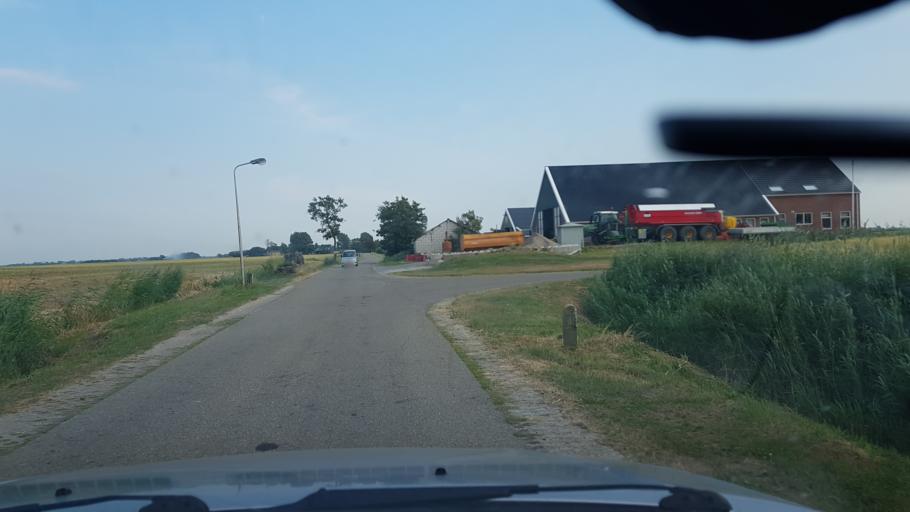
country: NL
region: Friesland
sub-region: Gemeente Dongeradeel
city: Holwerd
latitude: 53.3552
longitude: 5.8715
